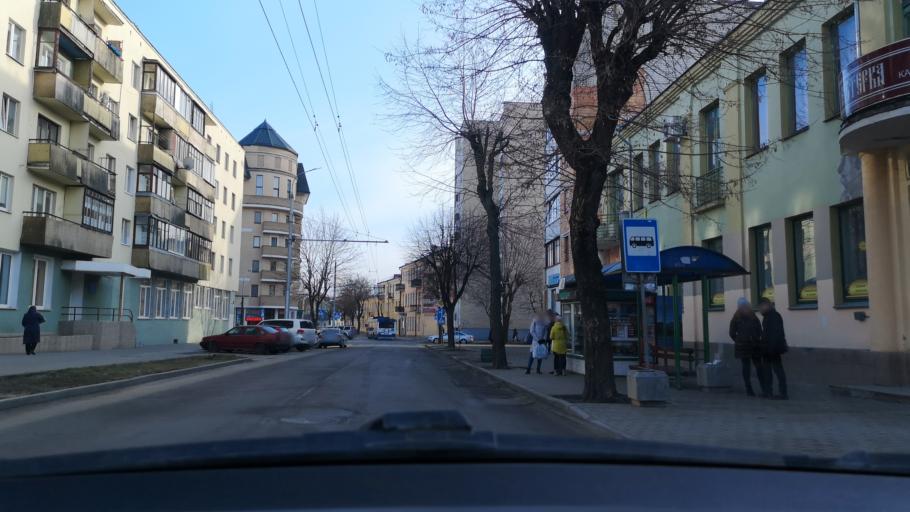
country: BY
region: Brest
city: Brest
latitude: 52.0942
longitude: 23.6892
